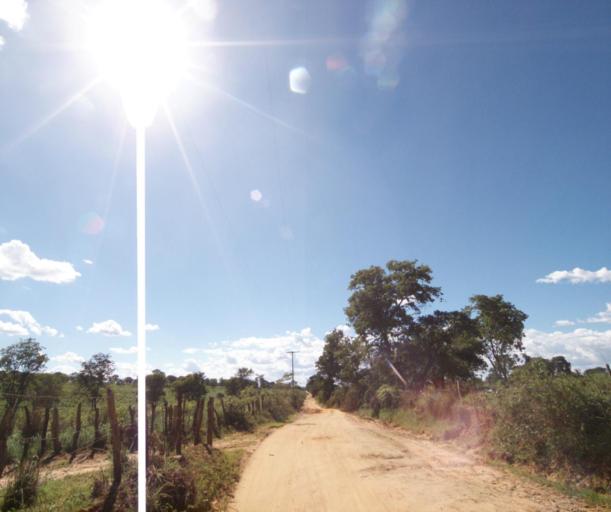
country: BR
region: Bahia
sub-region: Carinhanha
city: Carinhanha
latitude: -14.1834
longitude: -44.5038
